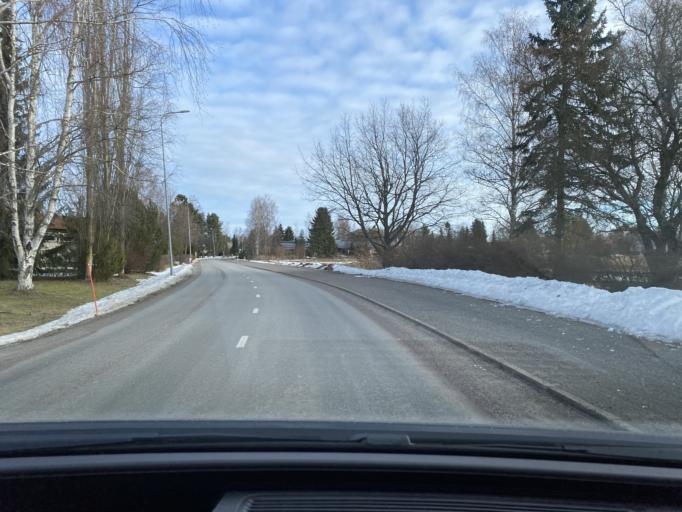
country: FI
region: Satakunta
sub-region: Pori
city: Huittinen
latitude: 61.1692
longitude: 22.6921
